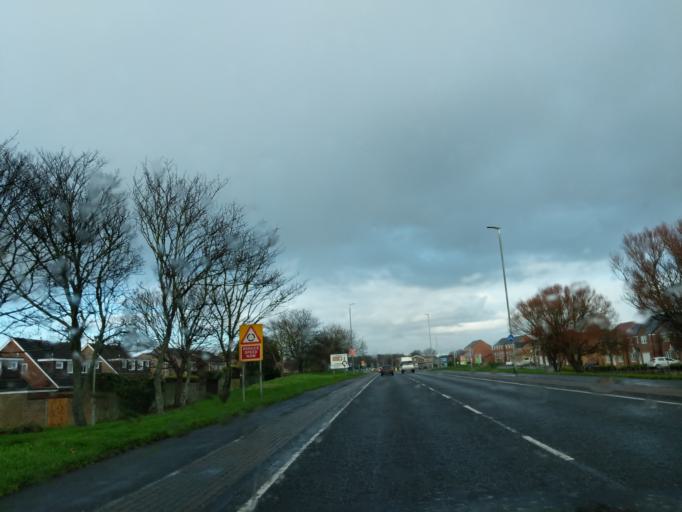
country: GB
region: England
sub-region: Northumberland
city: Blyth
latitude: 55.1132
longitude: -1.5058
